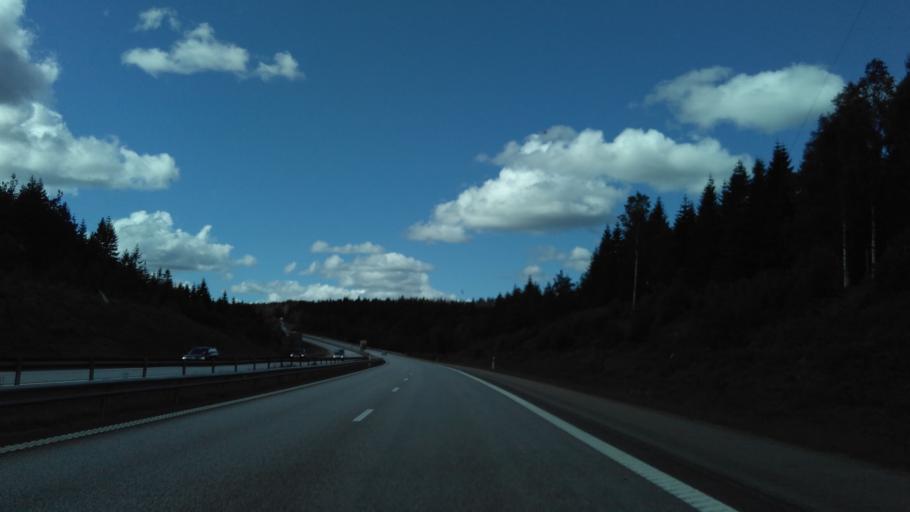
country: SE
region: Vaestra Goetaland
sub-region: Harryda Kommun
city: Hindas
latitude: 57.6748
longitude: 12.4738
